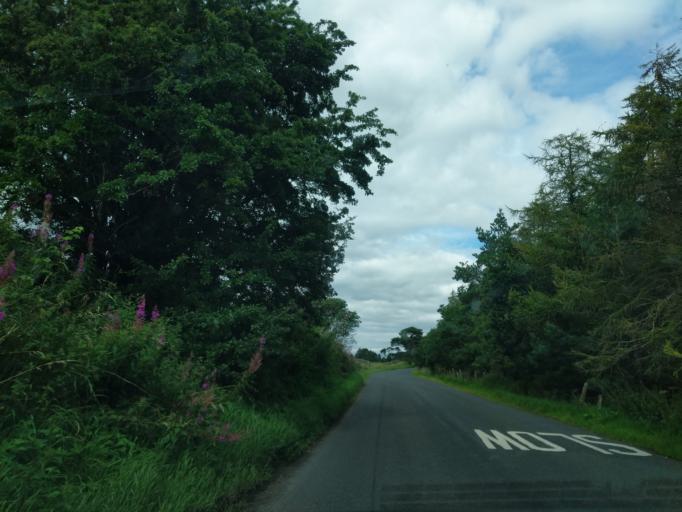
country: GB
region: Scotland
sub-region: The Scottish Borders
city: Peebles
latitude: 55.6375
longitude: -3.2831
